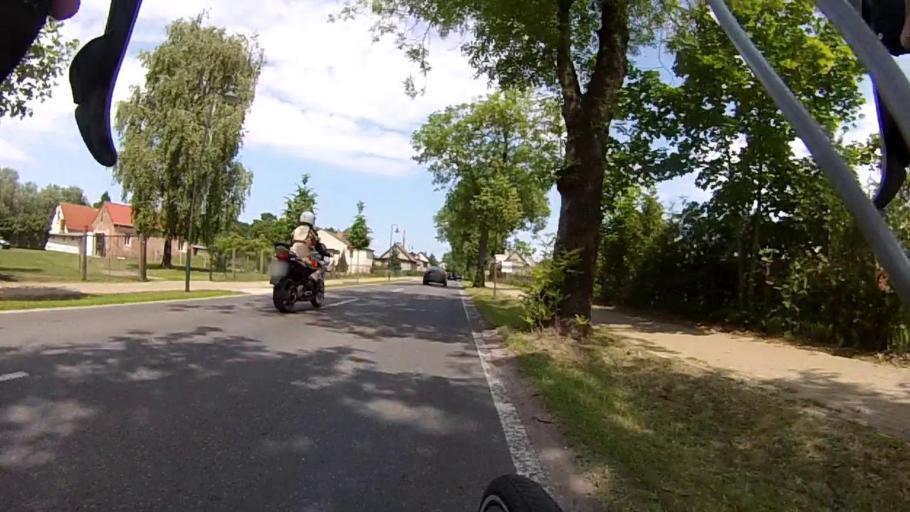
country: DE
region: Brandenburg
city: Liebenwalde
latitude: 52.8587
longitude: 13.3986
